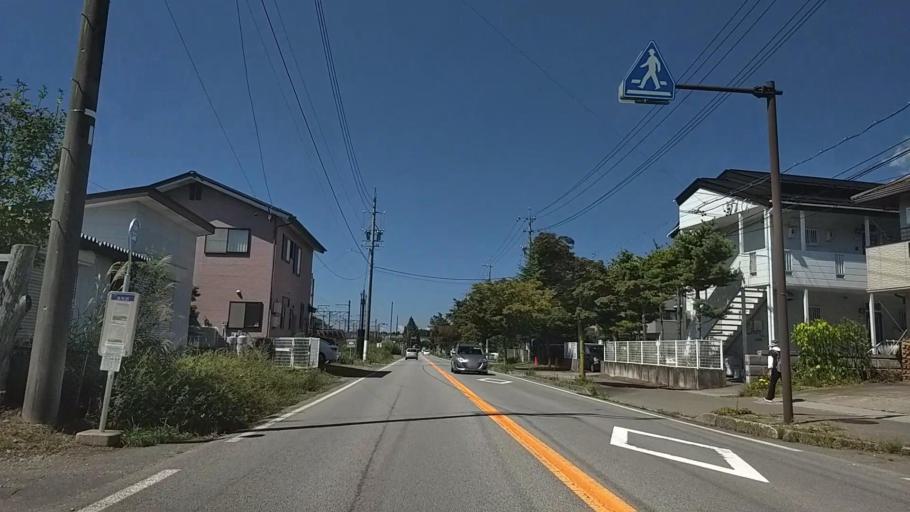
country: JP
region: Nagano
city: Saku
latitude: 36.3437
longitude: 138.6139
